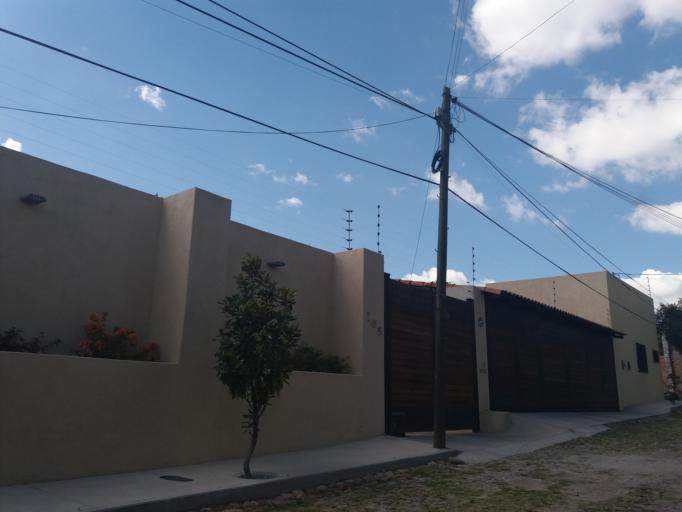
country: MX
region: Aguascalientes
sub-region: Aguascalientes
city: San Sebastian [Fraccionamiento]
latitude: 21.7899
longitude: -102.2780
